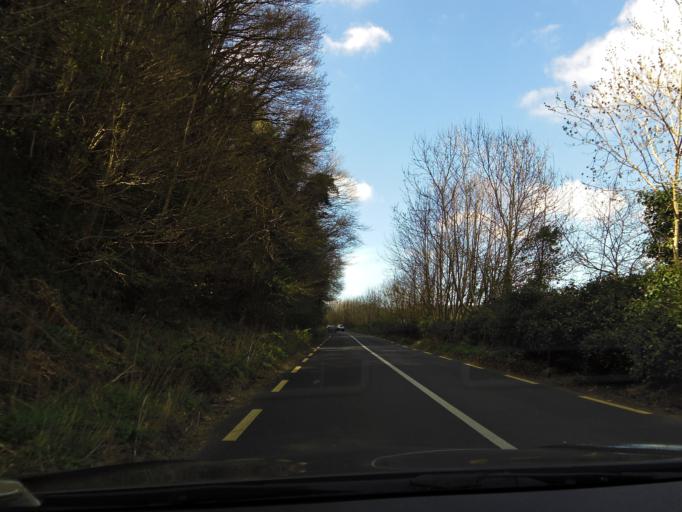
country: IE
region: Leinster
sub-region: Wicklow
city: Arklow
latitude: 52.8263
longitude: -6.2197
